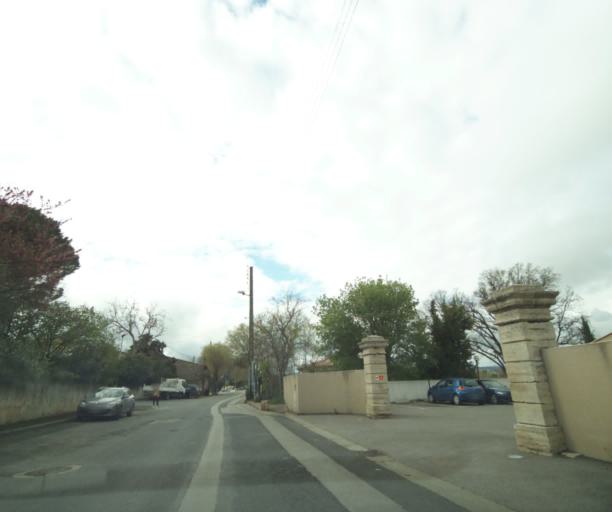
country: FR
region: Languedoc-Roussillon
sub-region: Departement de l'Herault
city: Fabregues
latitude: 43.5511
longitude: 3.7801
